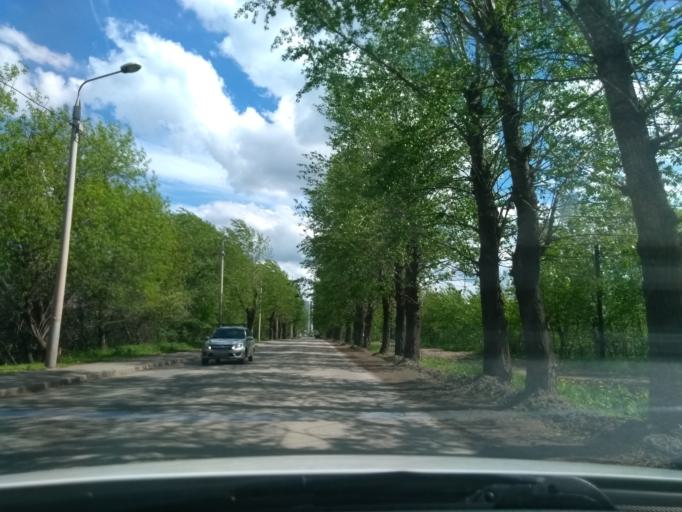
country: RU
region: Perm
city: Kondratovo
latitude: 58.0039
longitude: 56.1272
